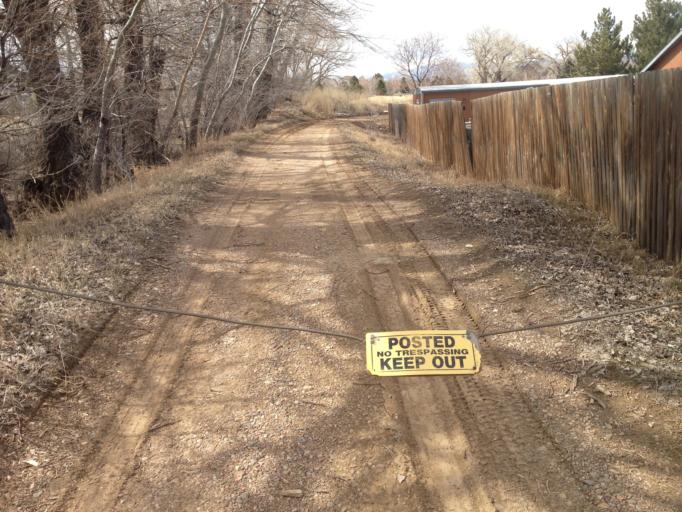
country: US
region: Colorado
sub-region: Boulder County
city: Louisville
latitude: 40.0068
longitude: -105.1313
